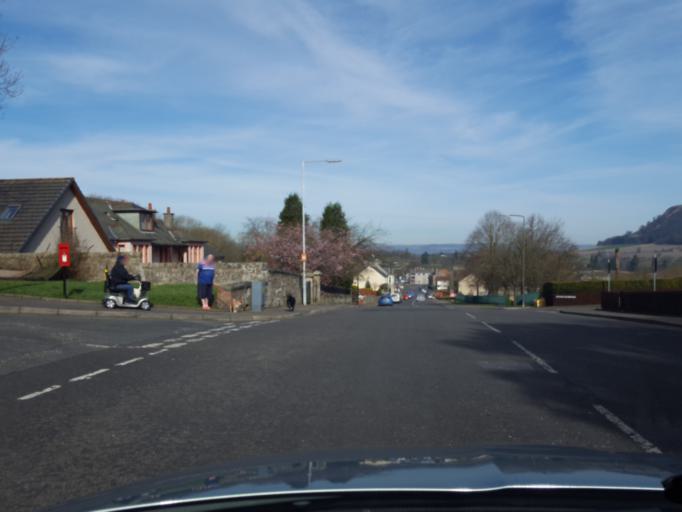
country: GB
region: Scotland
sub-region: Fife
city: Kelty
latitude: 56.1368
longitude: -3.3822
